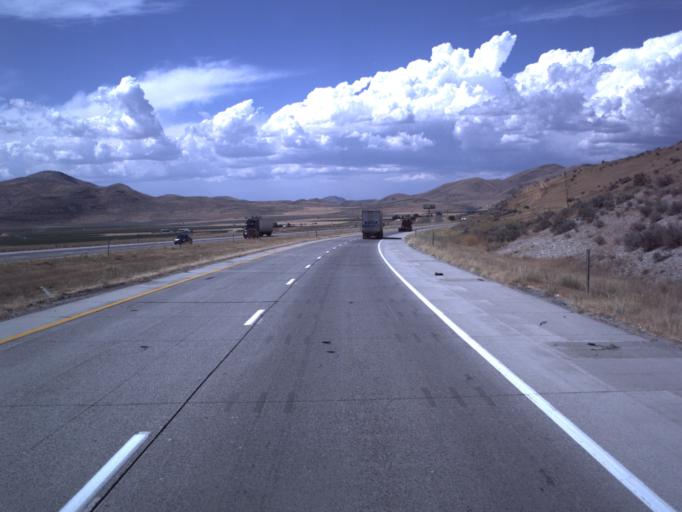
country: US
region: Utah
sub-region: Box Elder County
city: Garland
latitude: 41.7387
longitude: -112.2541
